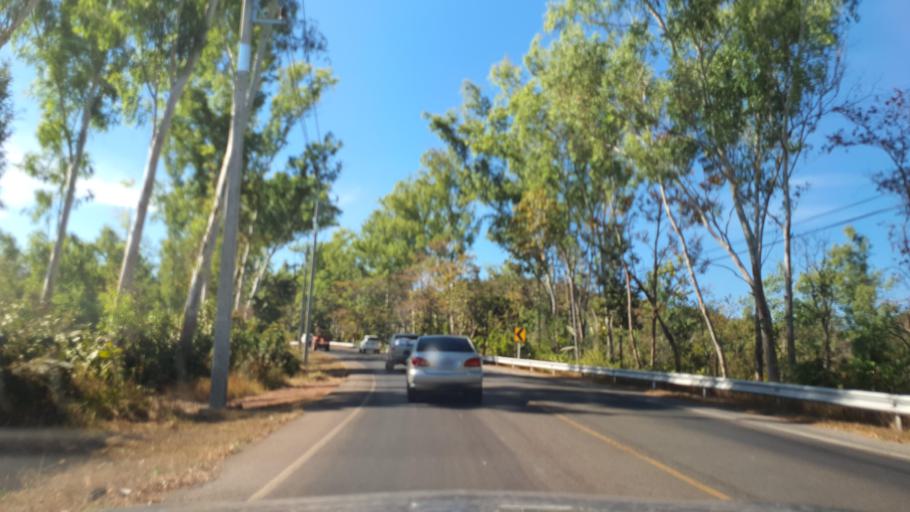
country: TH
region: Kalasin
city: Khao Wong
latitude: 16.7653
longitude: 104.1393
